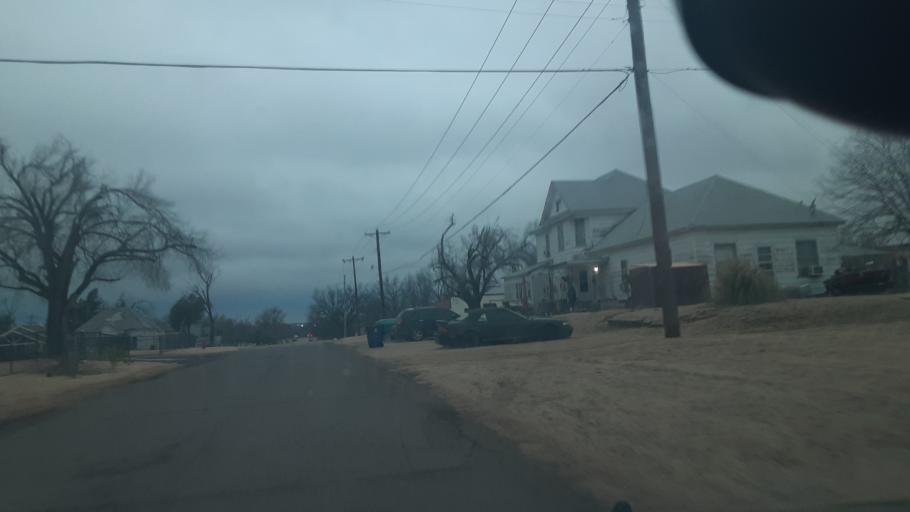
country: US
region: Oklahoma
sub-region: Logan County
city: Guthrie
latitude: 35.8760
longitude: -97.4116
